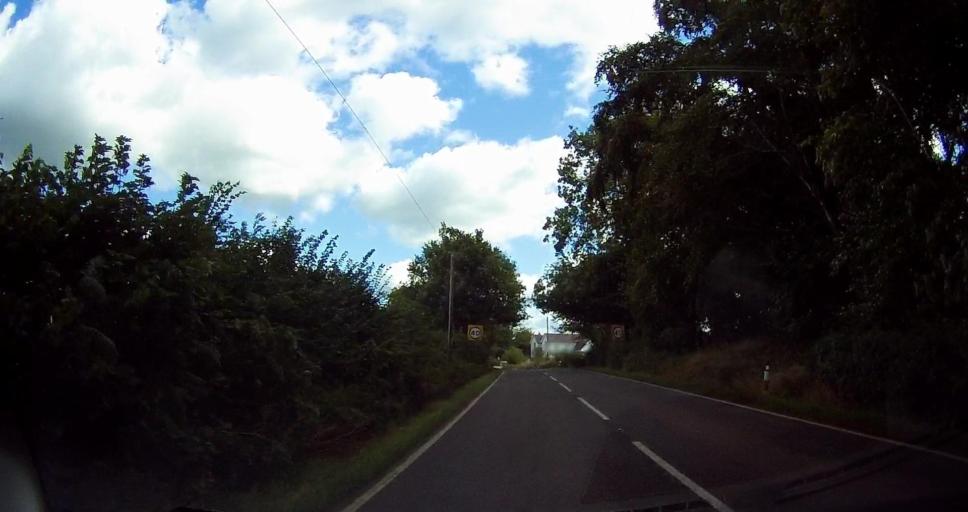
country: GB
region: England
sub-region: Cheshire East
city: Chorlton
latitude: 52.9806
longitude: -2.4192
